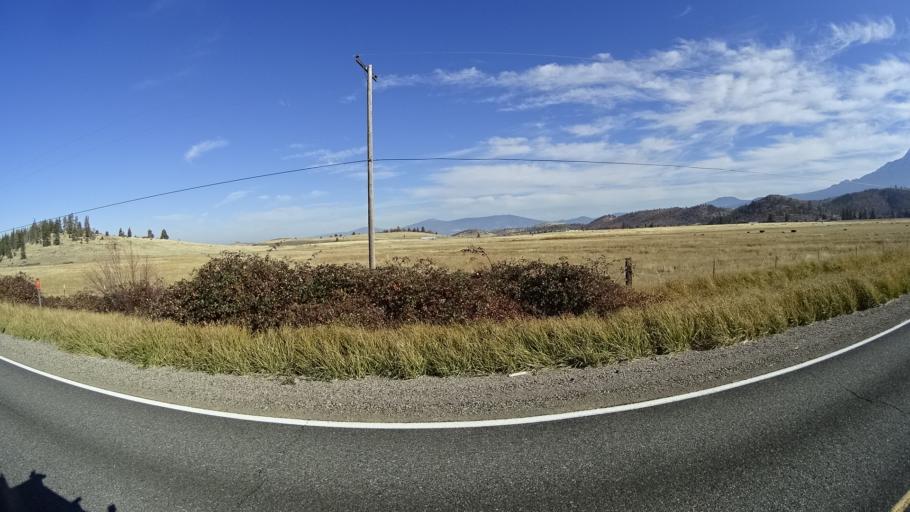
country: US
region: California
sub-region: Siskiyou County
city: Weed
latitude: 41.4455
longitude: -122.4453
